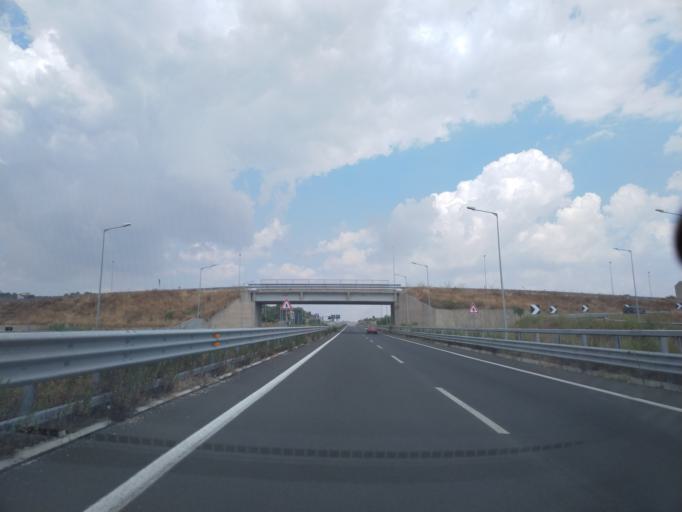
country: IT
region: Sicily
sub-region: Agrigento
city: Racalmuto
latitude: 37.3846
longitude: 13.7368
